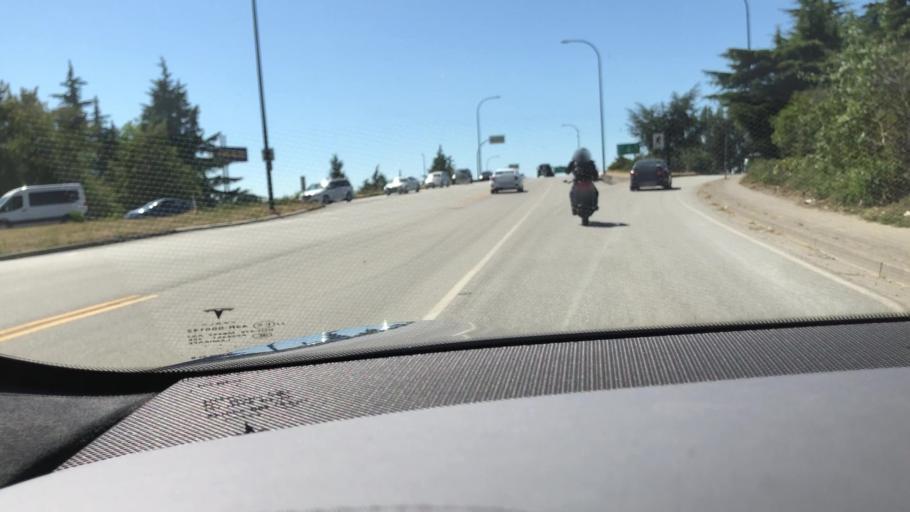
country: CA
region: British Columbia
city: Richmond
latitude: 49.1917
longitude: -123.0752
